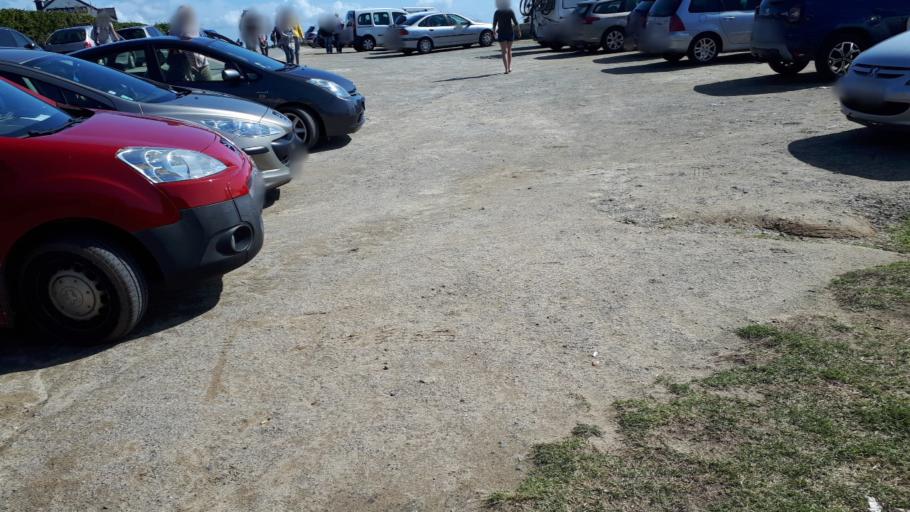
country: FR
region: Brittany
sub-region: Departement du Morbihan
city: Penestin
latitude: 47.4434
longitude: -2.4824
